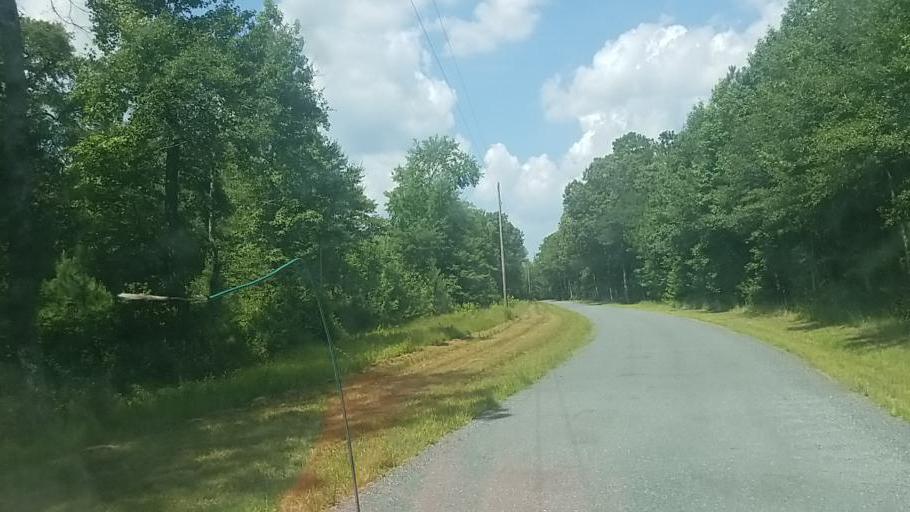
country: US
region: Maryland
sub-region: Worcester County
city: Snow Hill
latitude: 38.2475
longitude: -75.4168
